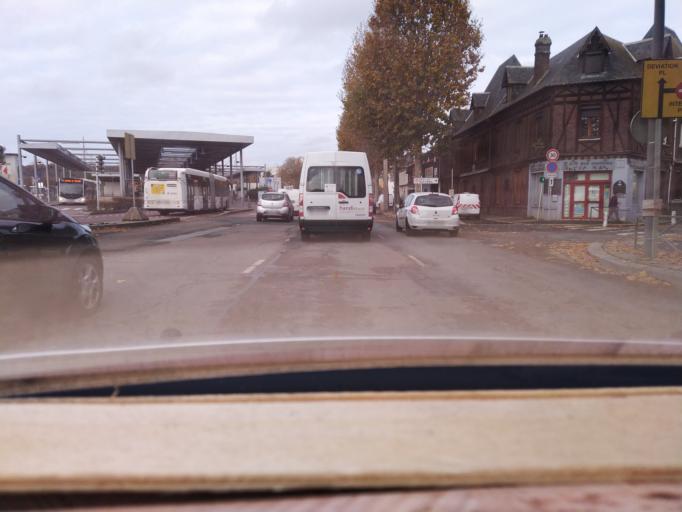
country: FR
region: Haute-Normandie
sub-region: Departement de la Seine-Maritime
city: Deville-les-Rouen
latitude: 49.4487
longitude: 1.0659
